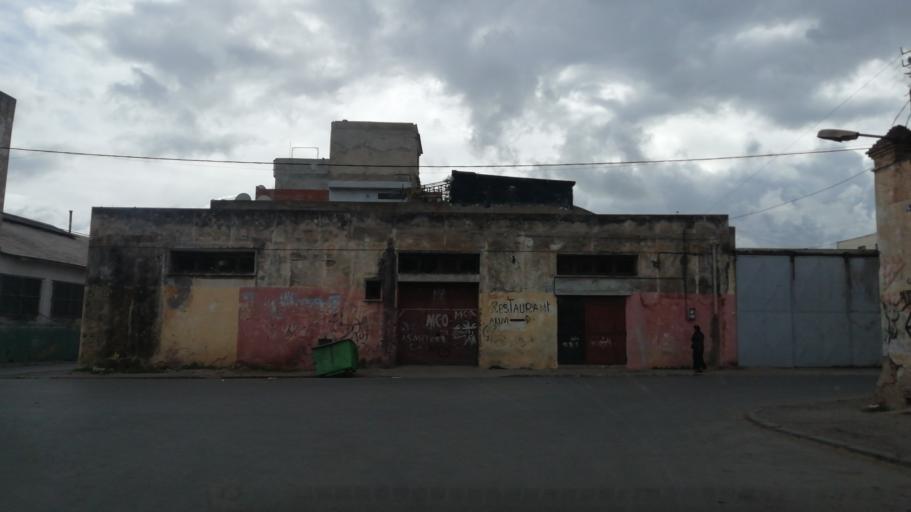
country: DZ
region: Oran
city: Oran
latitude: 35.6877
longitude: -0.6523
